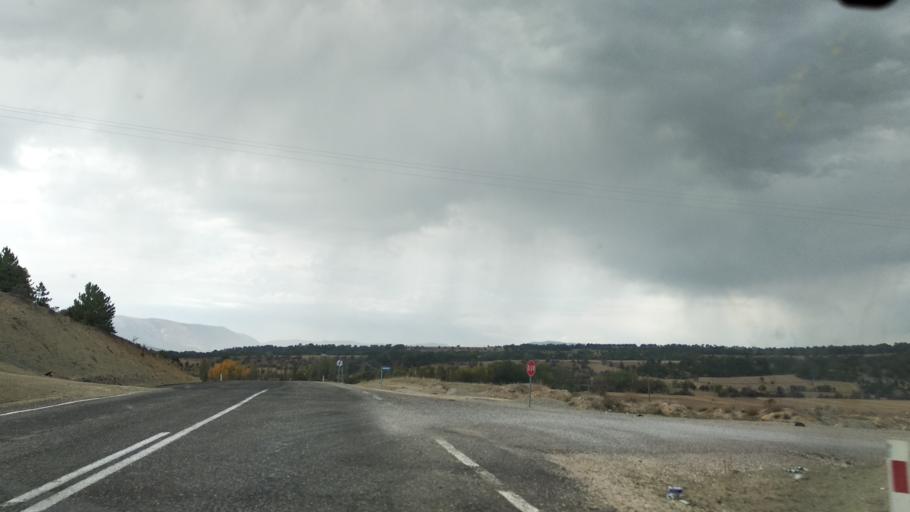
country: TR
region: Bolu
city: Seben
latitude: 40.3505
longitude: 31.4771
